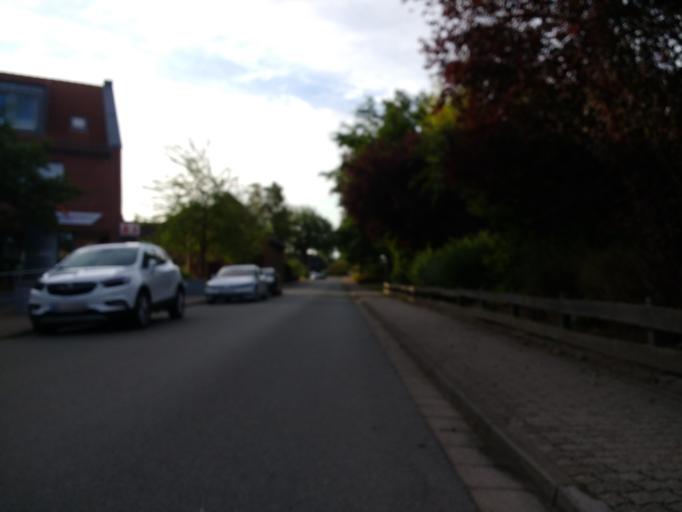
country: DE
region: Lower Saxony
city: Isenbuttel
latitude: 52.4376
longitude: 10.5785
